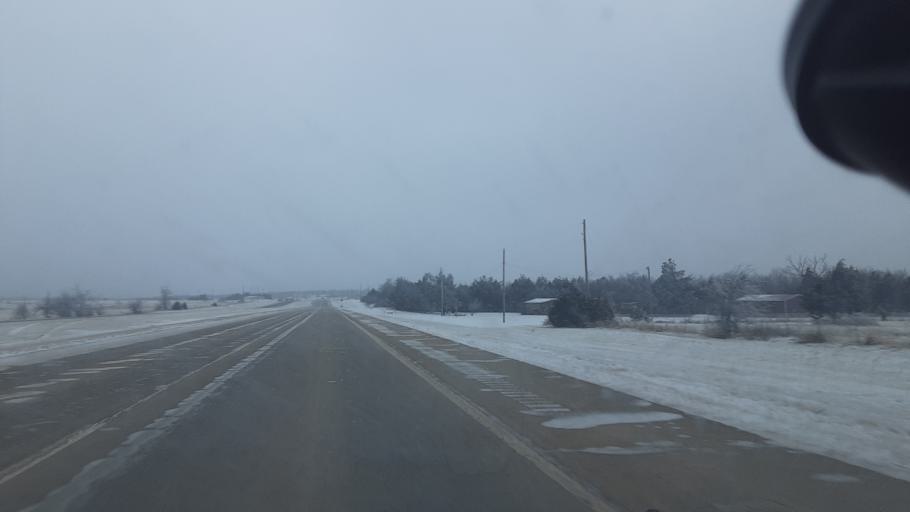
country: US
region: Oklahoma
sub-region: Logan County
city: Langston
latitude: 35.9119
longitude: -97.3328
